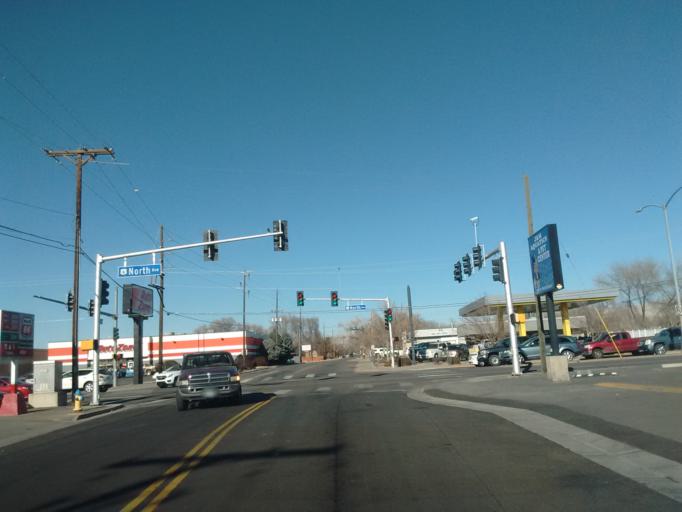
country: US
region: Colorado
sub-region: Mesa County
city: Fruitvale
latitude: 39.0771
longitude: -108.5244
